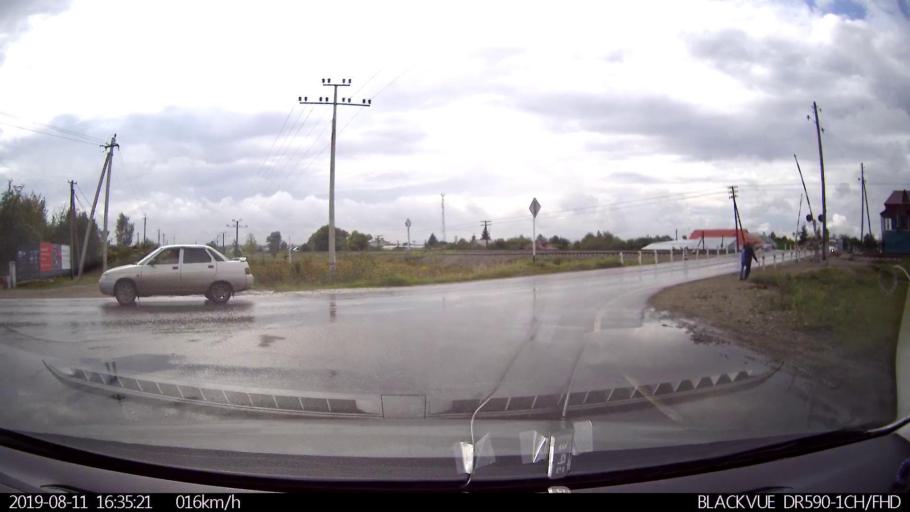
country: RU
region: Ulyanovsk
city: Mayna
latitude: 54.1149
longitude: 47.6156
